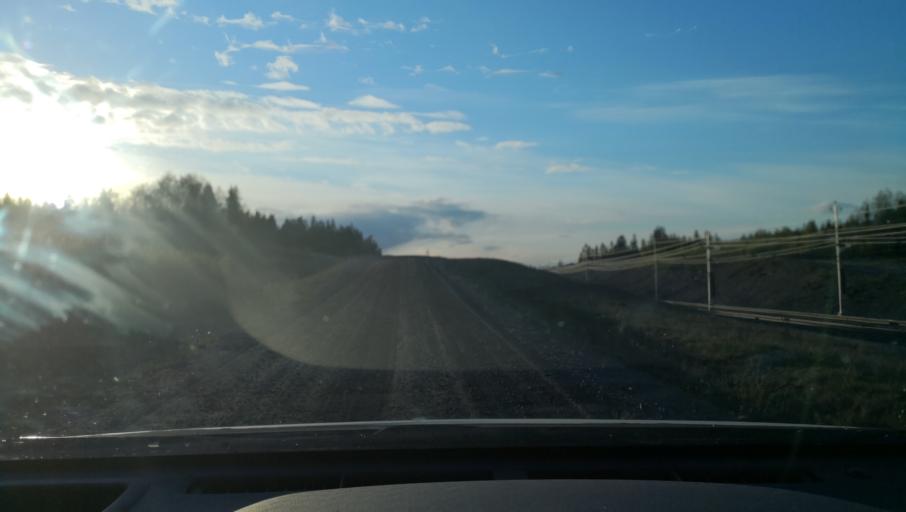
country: SE
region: OErebro
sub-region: Askersunds Kommun
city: Asbro
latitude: 58.8798
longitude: 15.1406
